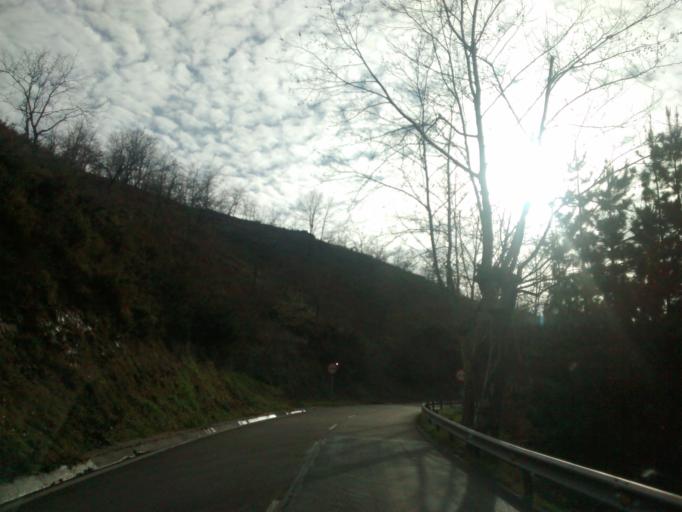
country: ES
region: Cantabria
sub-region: Provincia de Cantabria
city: Ruente
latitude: 43.2571
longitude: -4.3448
